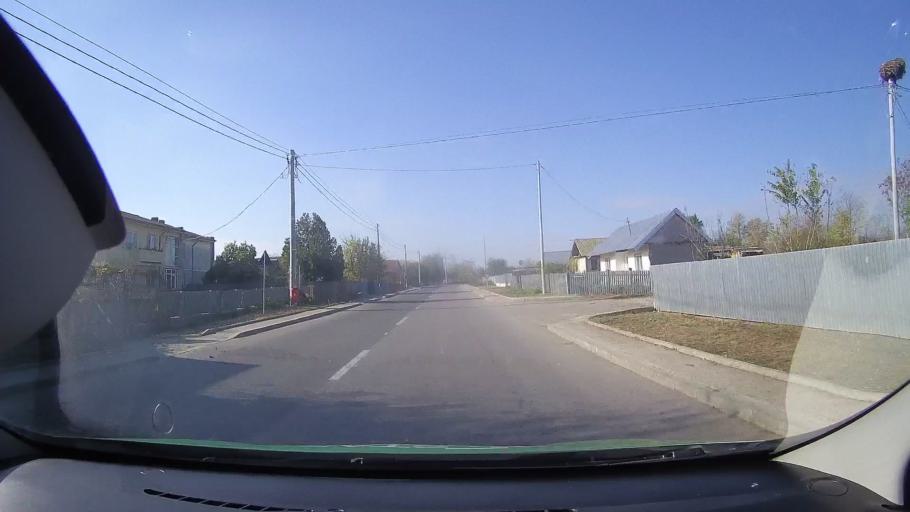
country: RO
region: Tulcea
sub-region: Comuna Mahmudia
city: Mahmudia
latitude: 45.0090
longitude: 29.0607
